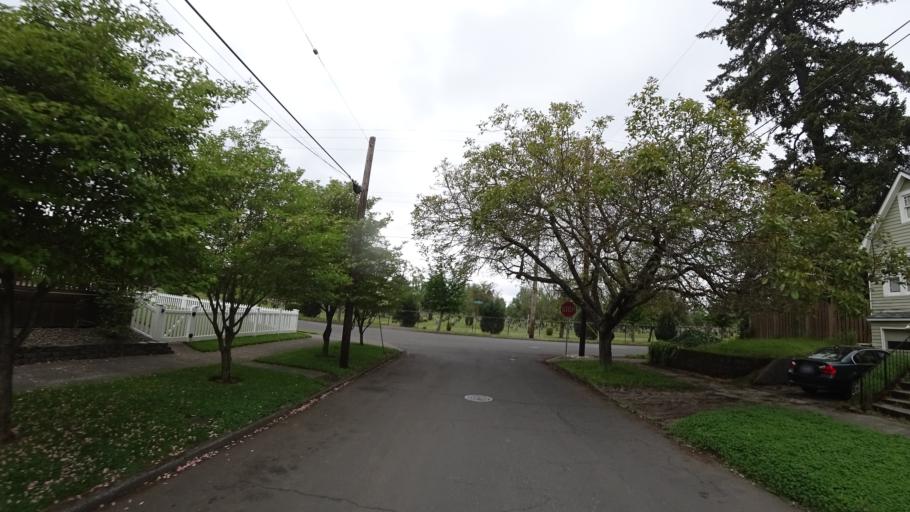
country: US
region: Oregon
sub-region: Multnomah County
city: Portland
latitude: 45.5480
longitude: -122.6087
